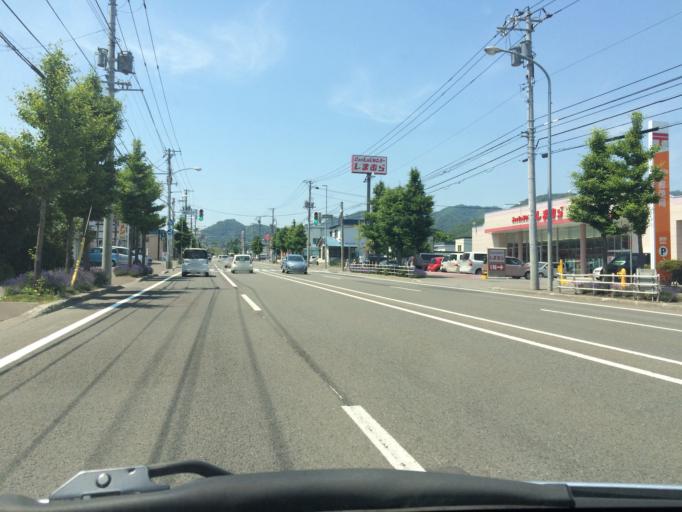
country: JP
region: Hokkaido
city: Sapporo
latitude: 42.9618
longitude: 141.2924
